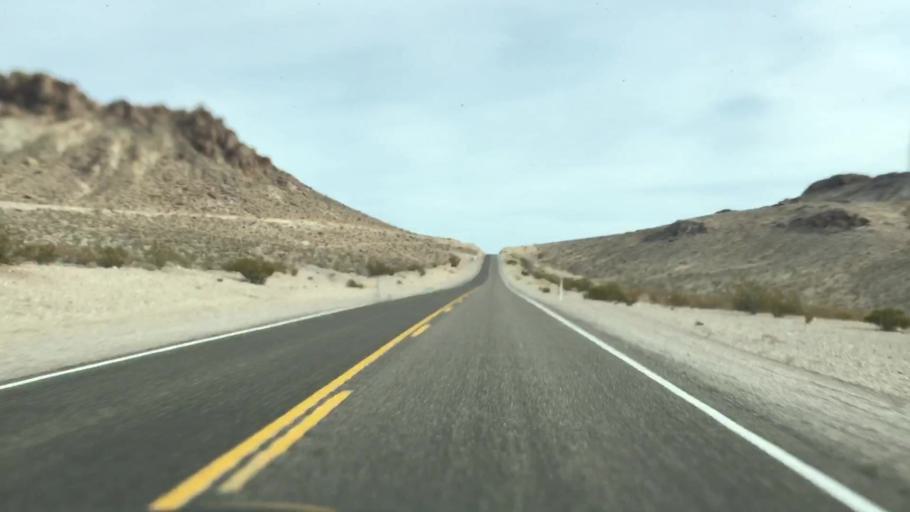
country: US
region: Nevada
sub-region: Nye County
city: Beatty
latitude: 36.8964
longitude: -116.7982
